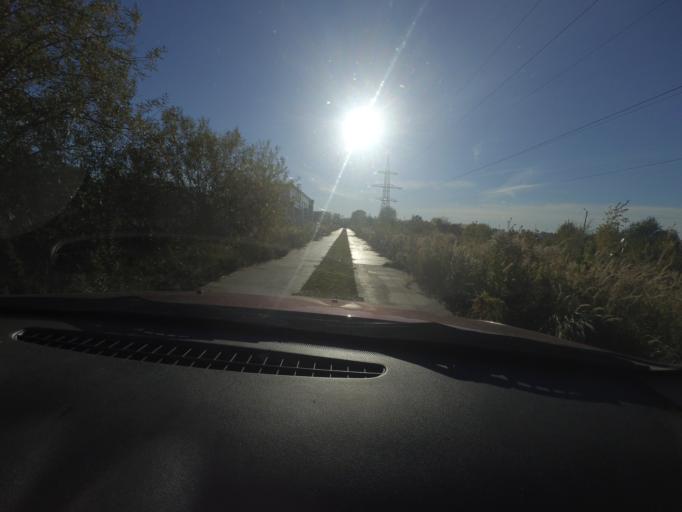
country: RU
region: Nizjnij Novgorod
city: Bor
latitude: 56.3113
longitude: 44.0662
